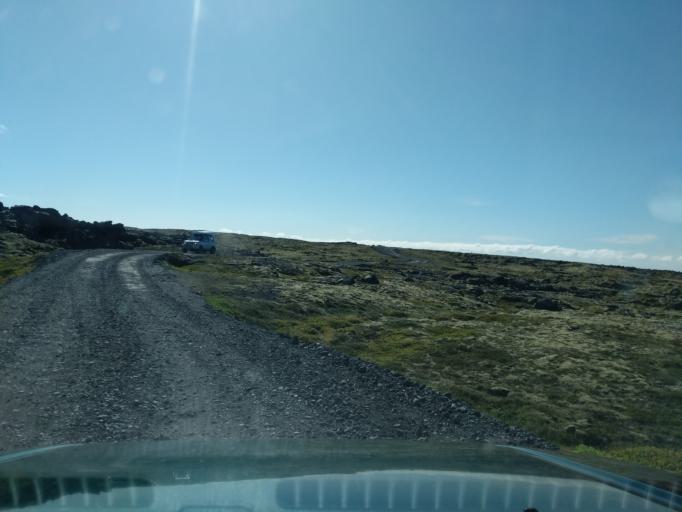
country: IS
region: West
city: Olafsvik
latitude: 64.8742
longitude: -24.0140
